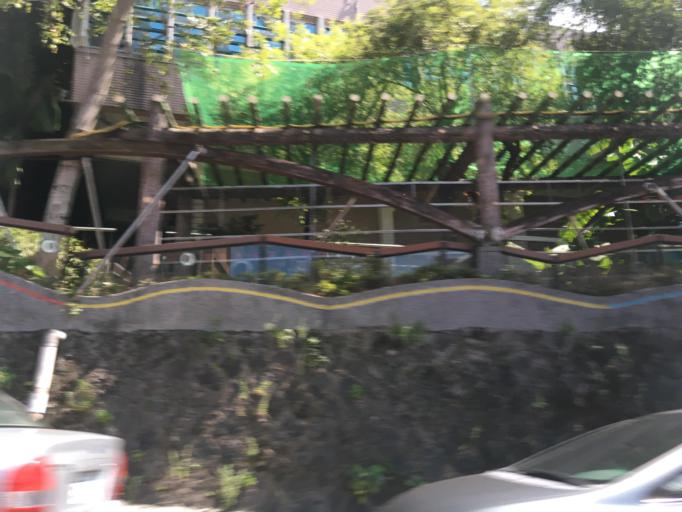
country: TW
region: Taipei
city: Taipei
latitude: 25.1440
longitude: 121.5018
